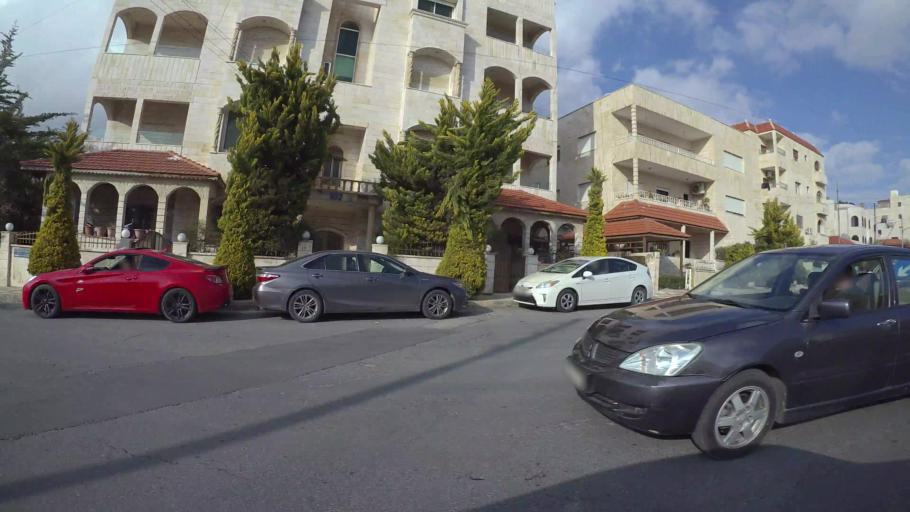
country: JO
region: Amman
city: Wadi as Sir
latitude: 31.9812
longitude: 35.8456
